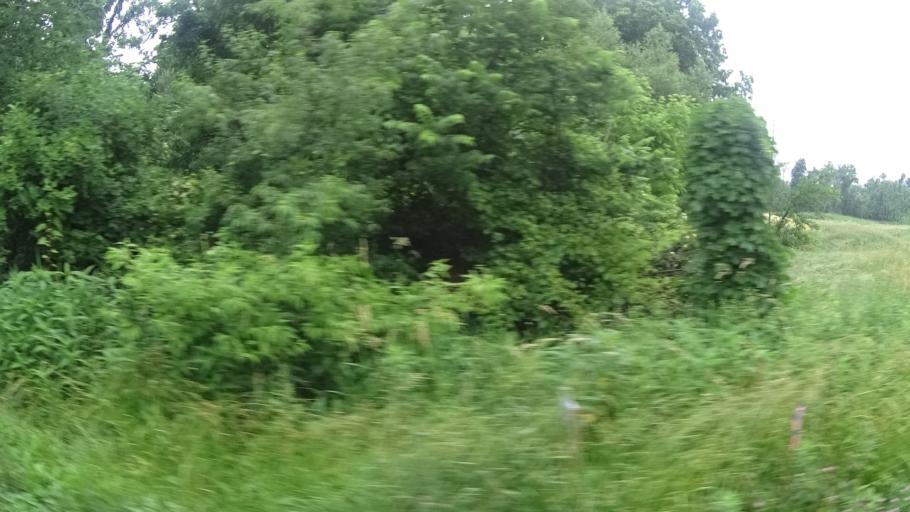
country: US
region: Ohio
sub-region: Erie County
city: Milan
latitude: 41.3352
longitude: -82.5936
